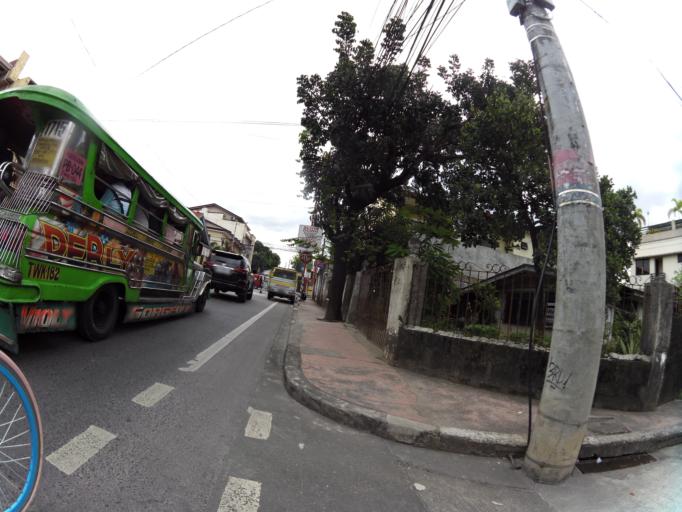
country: PH
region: Calabarzon
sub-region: Province of Rizal
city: Antipolo
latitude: 14.6412
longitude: 121.1133
